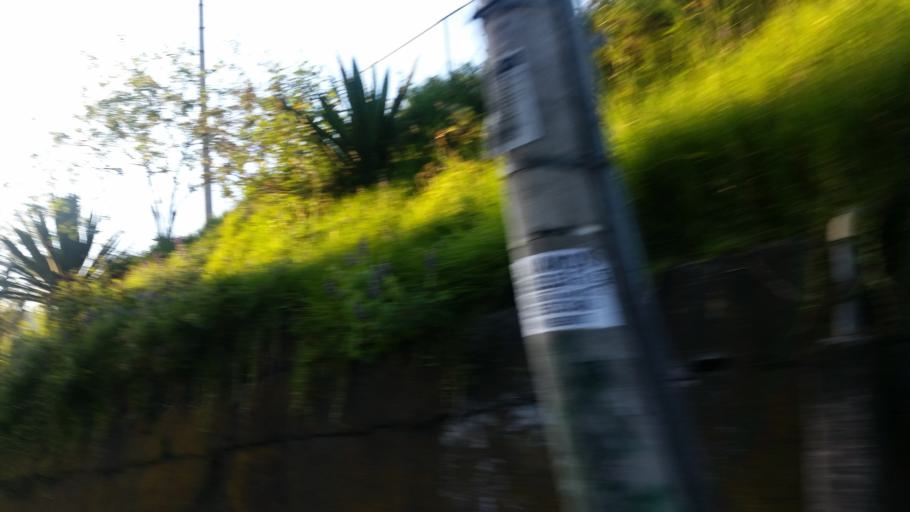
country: EC
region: Pichincha
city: Quito
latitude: -0.2133
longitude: -78.4830
